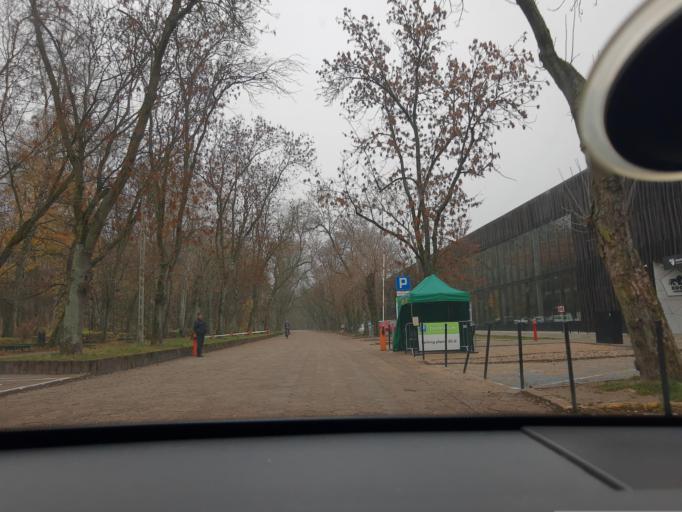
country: PL
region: Lodz Voivodeship
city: Lodz
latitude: 51.7639
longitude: 19.4125
